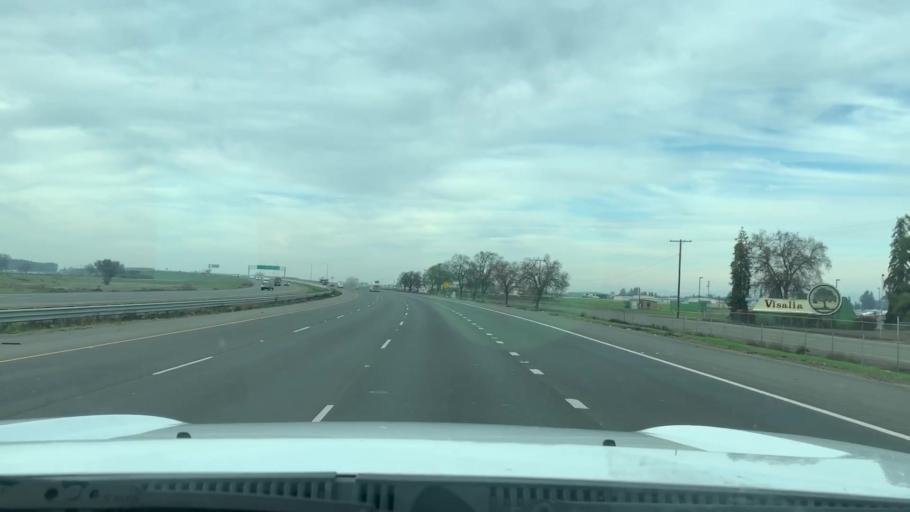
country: US
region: California
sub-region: Tulare County
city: Goshen
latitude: 36.3132
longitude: -119.3938
